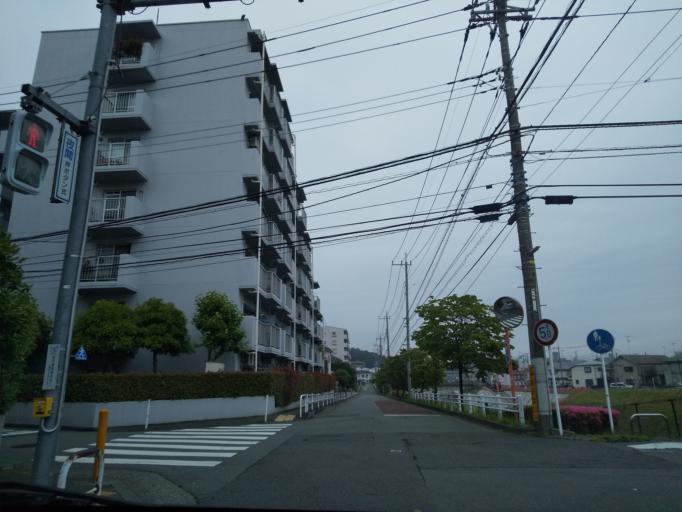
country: JP
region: Tokyo
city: Hino
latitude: 35.6467
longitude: 139.4329
